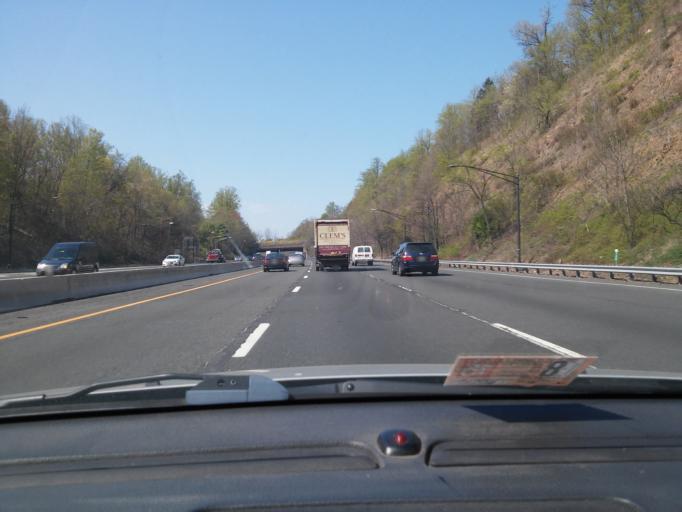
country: US
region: New Jersey
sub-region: Union County
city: Mountainside
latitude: 40.6964
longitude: -74.3701
